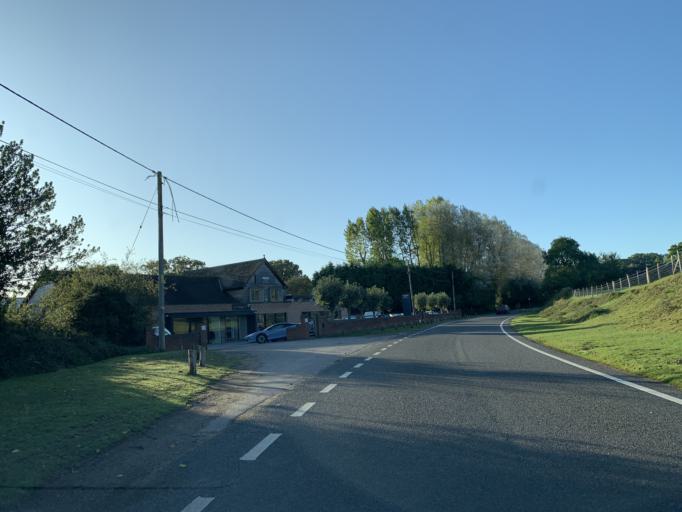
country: GB
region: England
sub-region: Hampshire
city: West Wellow
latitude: 50.9451
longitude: -1.6179
